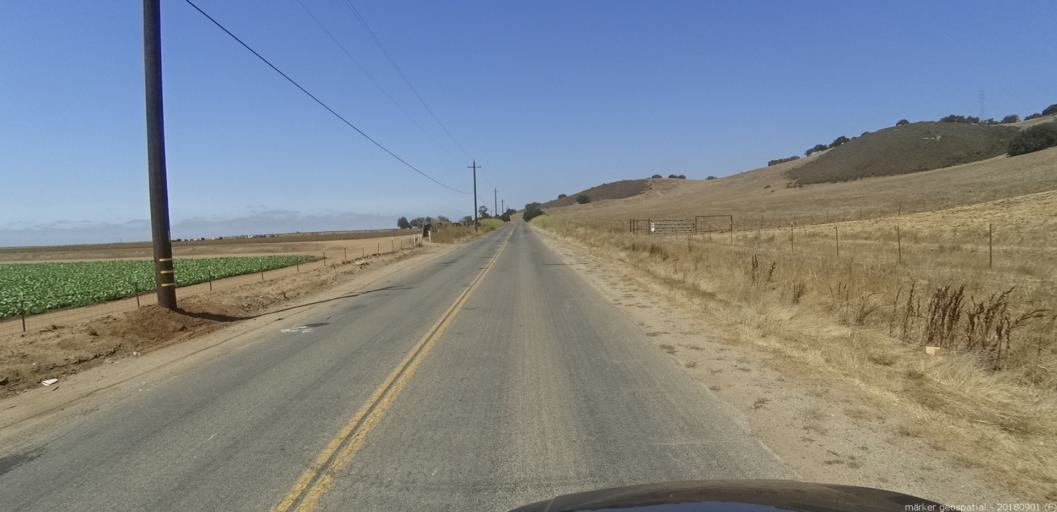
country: US
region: California
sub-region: Monterey County
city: Salinas
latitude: 36.6855
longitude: -121.5630
